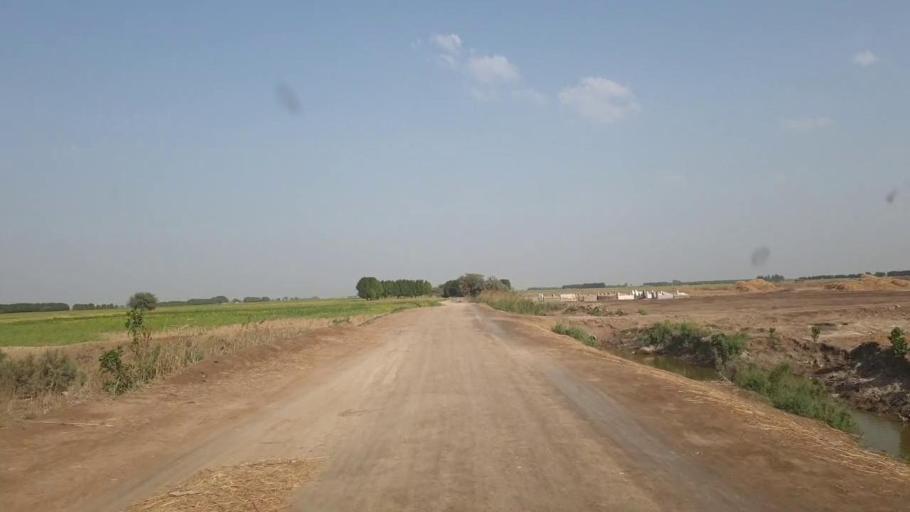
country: PK
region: Sindh
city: Kario
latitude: 24.5822
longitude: 68.5417
